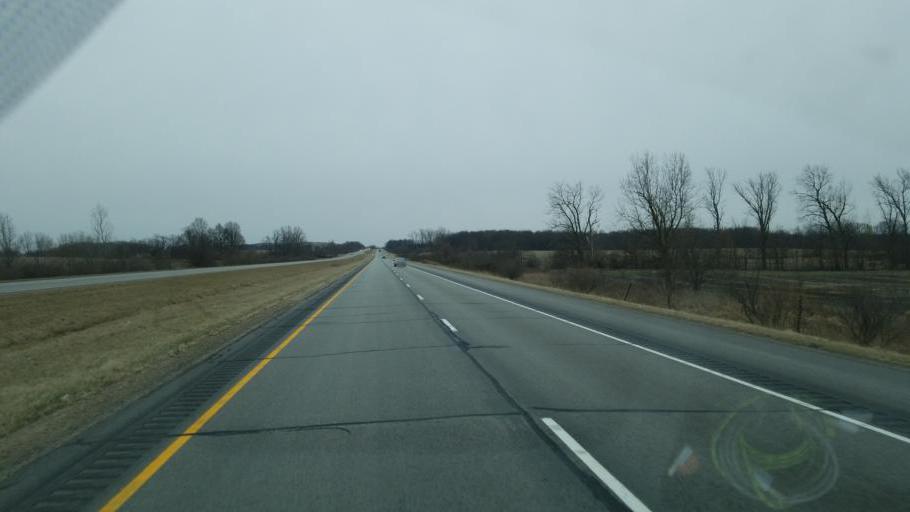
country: US
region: Indiana
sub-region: Marshall County
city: Argos
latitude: 41.1947
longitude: -86.2536
